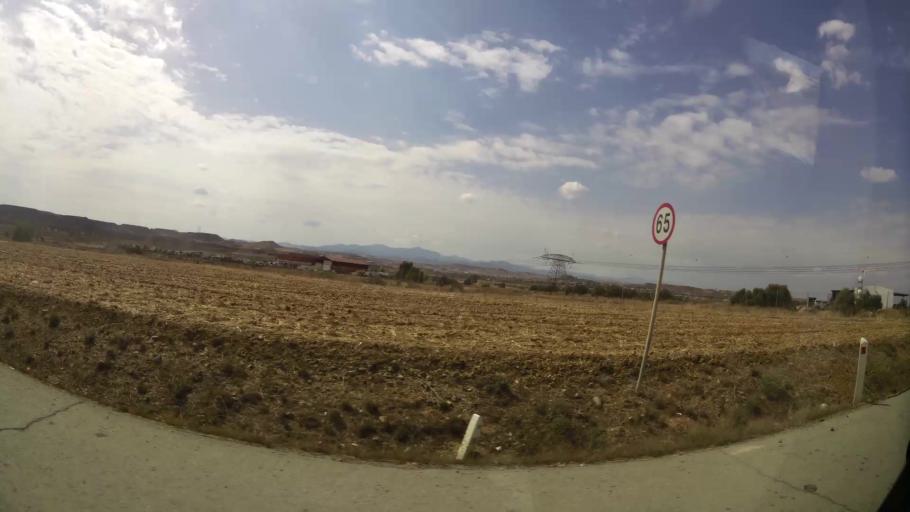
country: CY
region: Lefkosia
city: Tseri
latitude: 35.0633
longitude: 33.3443
